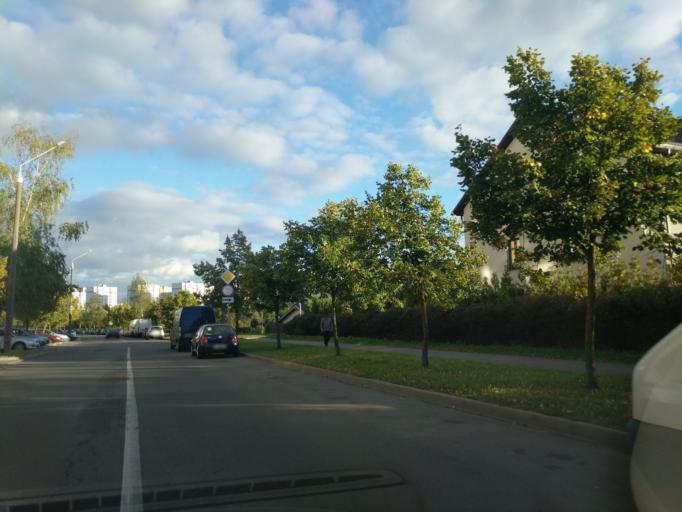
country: BY
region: Minsk
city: Malinovka
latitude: 53.8565
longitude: 27.4575
